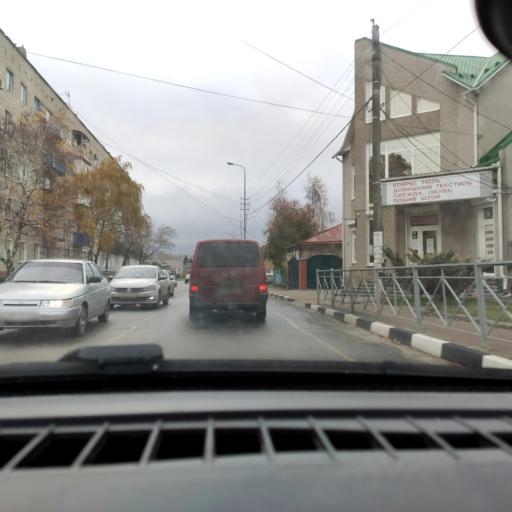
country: RU
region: Belgorod
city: Alekseyevka
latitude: 50.6277
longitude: 38.6889
